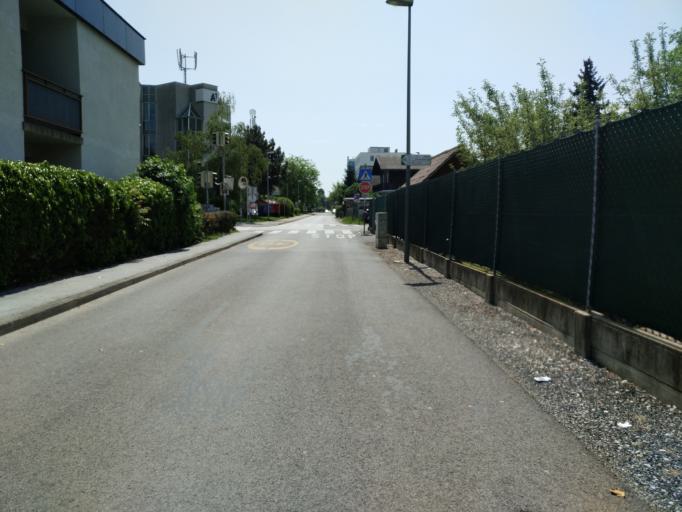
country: AT
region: Styria
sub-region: Graz Stadt
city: Goesting
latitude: 47.0977
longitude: 15.4083
